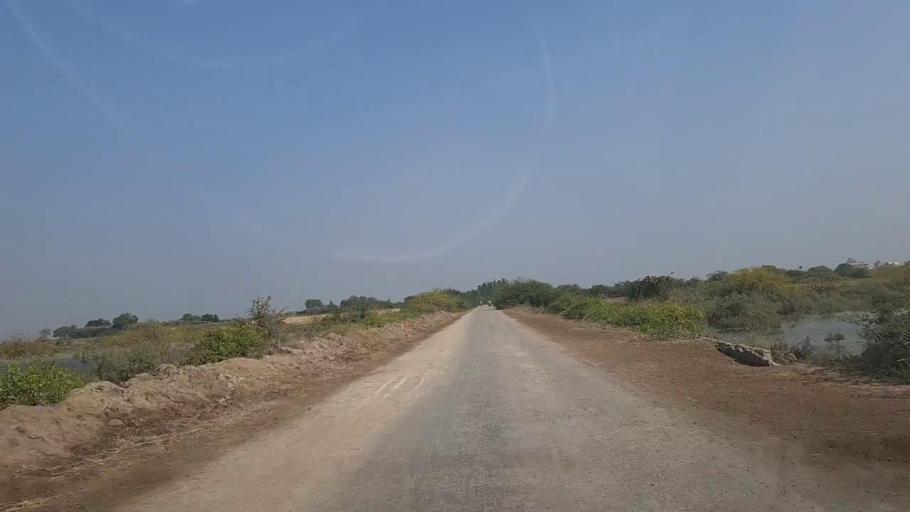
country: PK
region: Sindh
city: Keti Bandar
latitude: 24.2497
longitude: 67.7186
